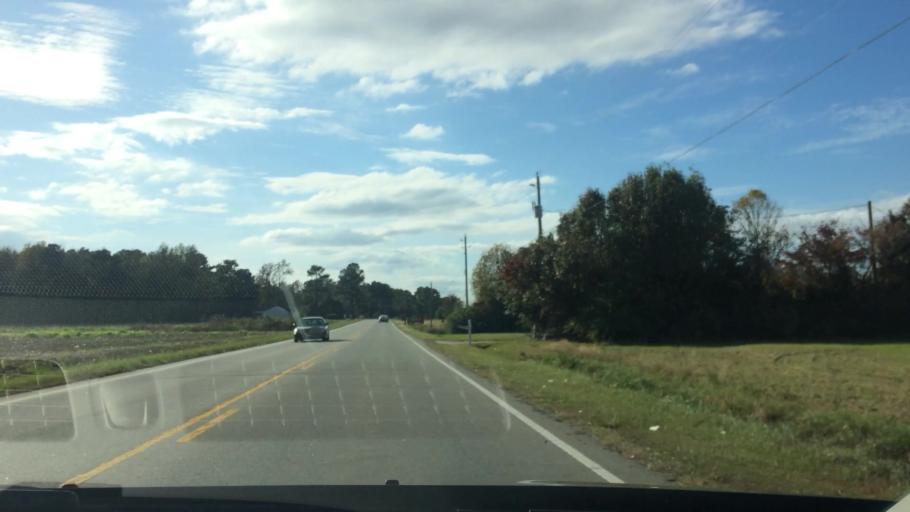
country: US
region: North Carolina
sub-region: Wayne County
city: Elroy
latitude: 35.4407
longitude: -77.8297
